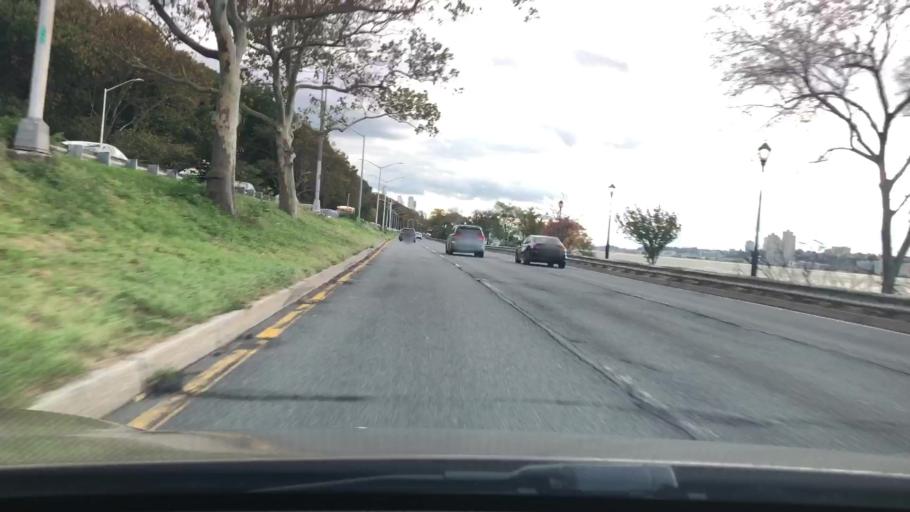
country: US
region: New Jersey
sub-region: Bergen County
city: Edgewater
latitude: 40.8114
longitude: -73.9669
